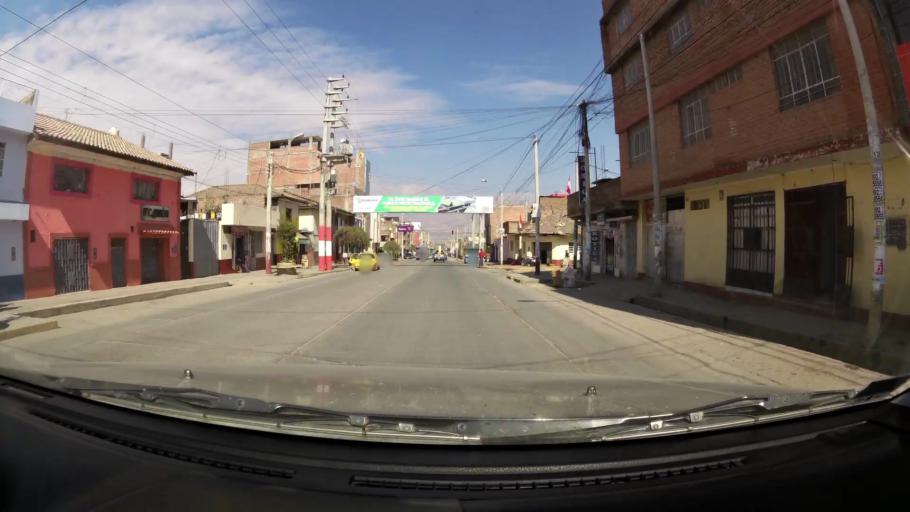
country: PE
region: Junin
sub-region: Provincia de Huancayo
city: El Tambo
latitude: -12.0722
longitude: -75.2186
